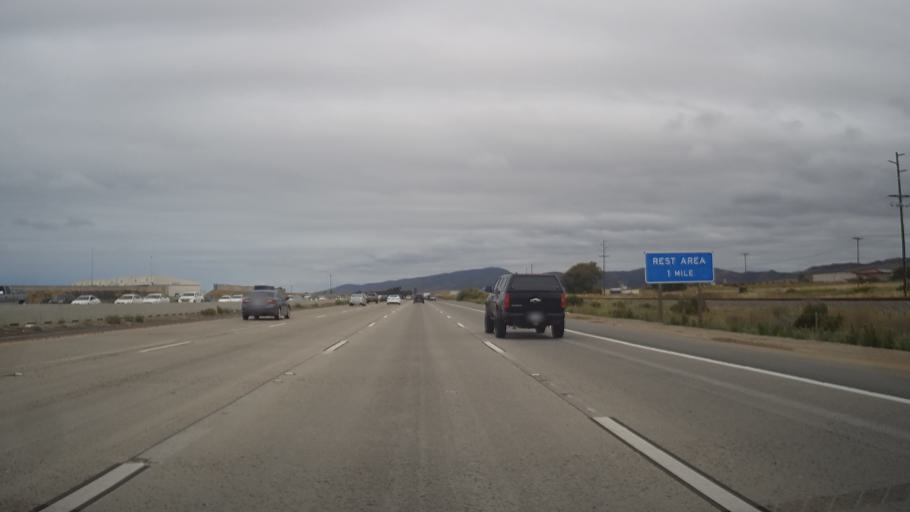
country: US
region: California
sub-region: San Diego County
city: Camp Pendleton South
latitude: 33.2577
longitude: -117.4260
